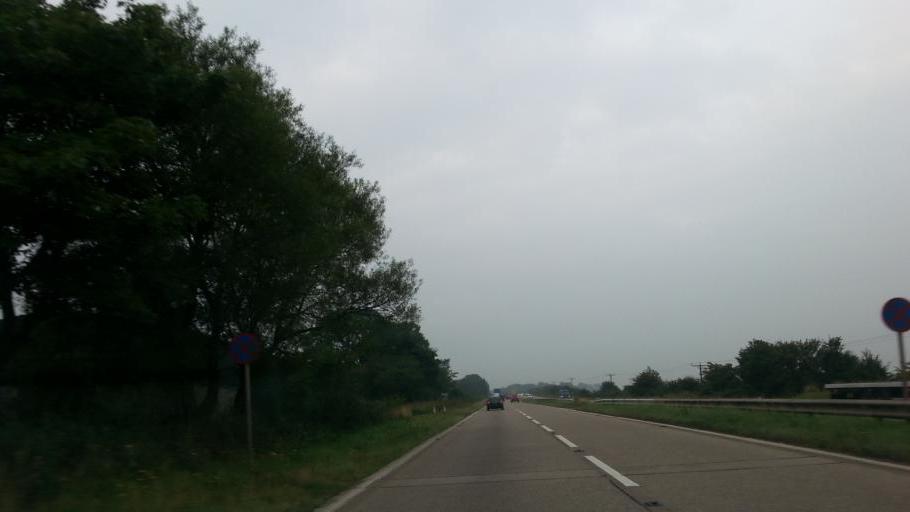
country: GB
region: England
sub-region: Nottinghamshire
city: Cotgrave
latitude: 52.8399
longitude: -1.0349
